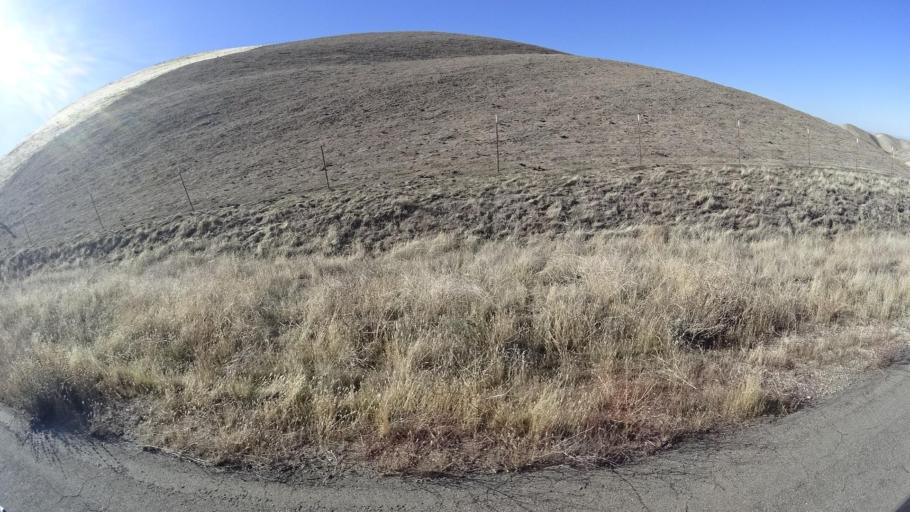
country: US
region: California
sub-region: Kern County
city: Maricopa
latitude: 34.9535
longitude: -119.4065
